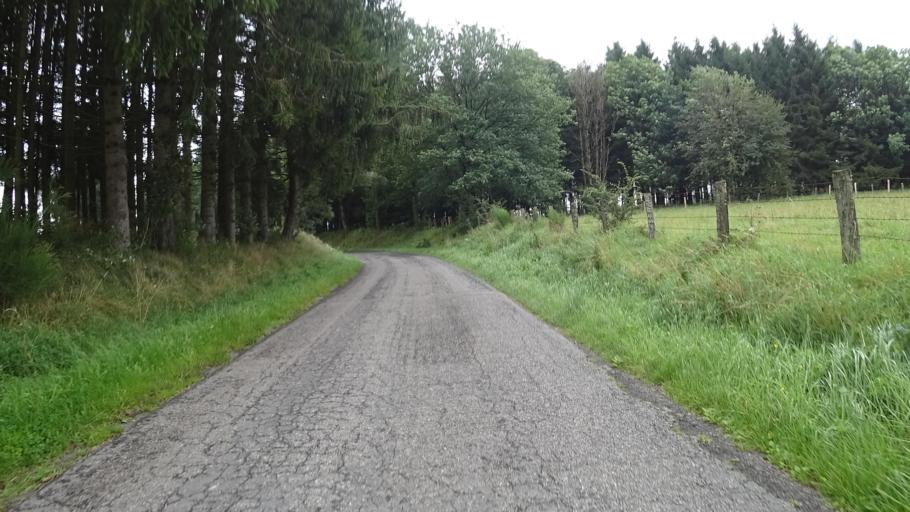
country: BE
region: Wallonia
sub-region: Province du Luxembourg
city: Chiny
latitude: 49.8088
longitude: 5.3359
